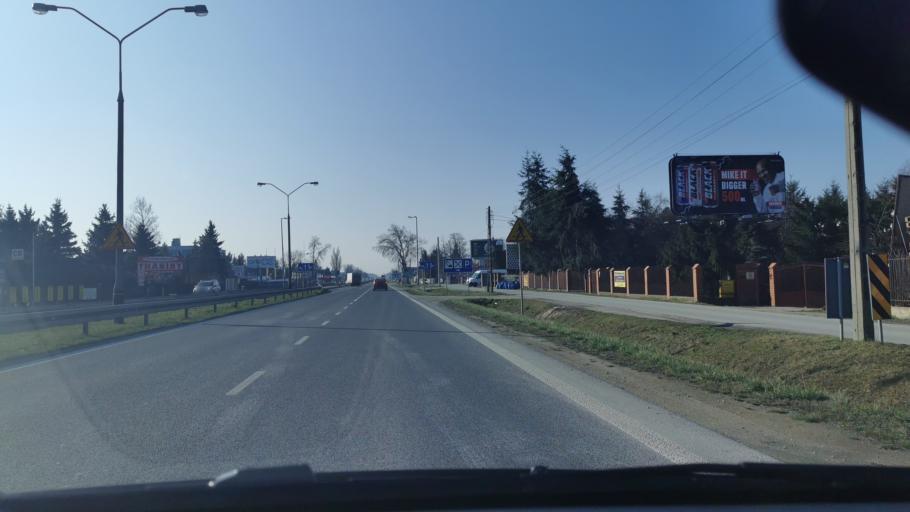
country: PL
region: Masovian Voivodeship
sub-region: Powiat pruszkowski
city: Nowe Grocholice
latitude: 52.1259
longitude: 20.8953
